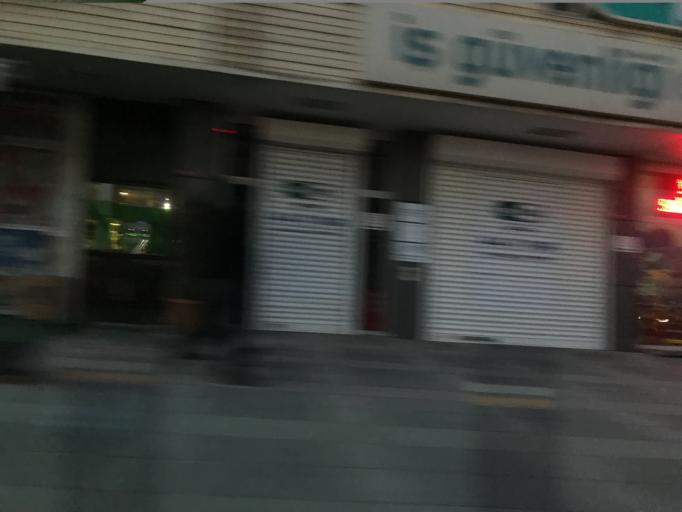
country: TR
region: Istanbul
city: Pendik
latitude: 40.9058
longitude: 29.2861
